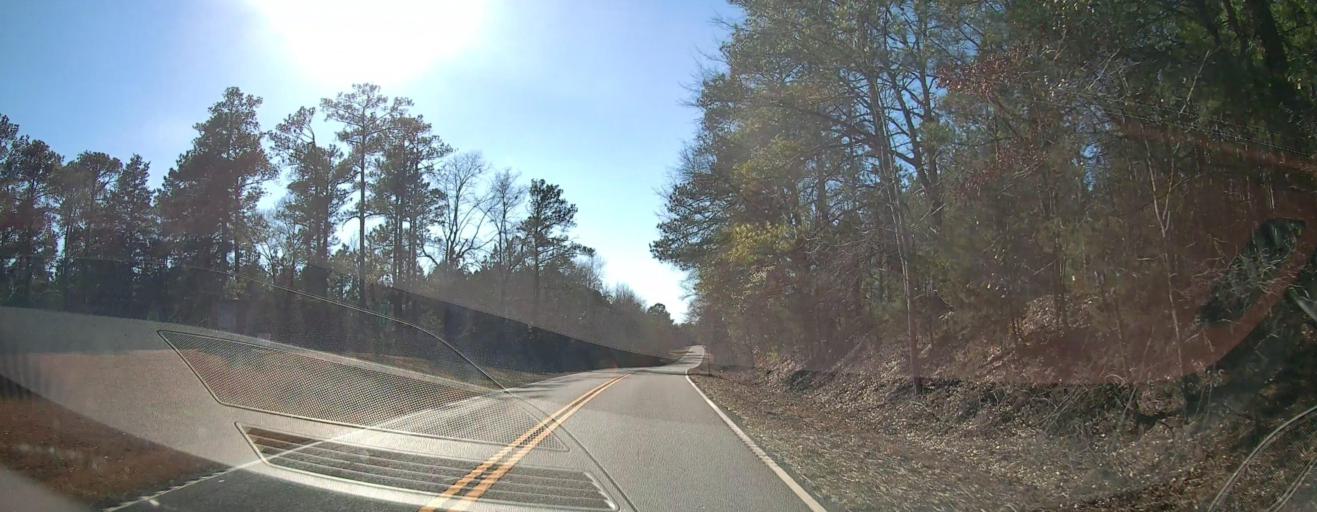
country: US
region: Georgia
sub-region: Taylor County
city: Butler
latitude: 32.6465
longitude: -84.3751
